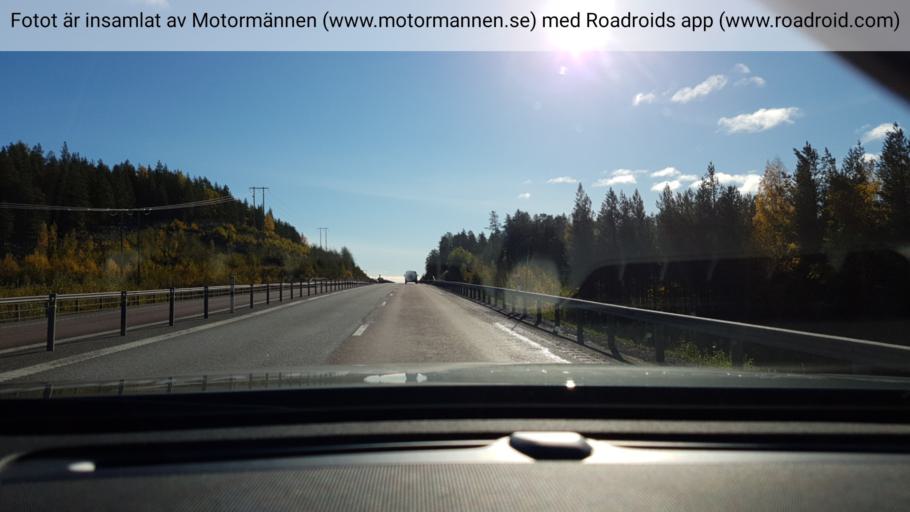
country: SE
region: Vaesterbotten
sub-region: Skelleftea Kommun
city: Soedra Bergsbyn
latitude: 64.6586
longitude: 21.1144
